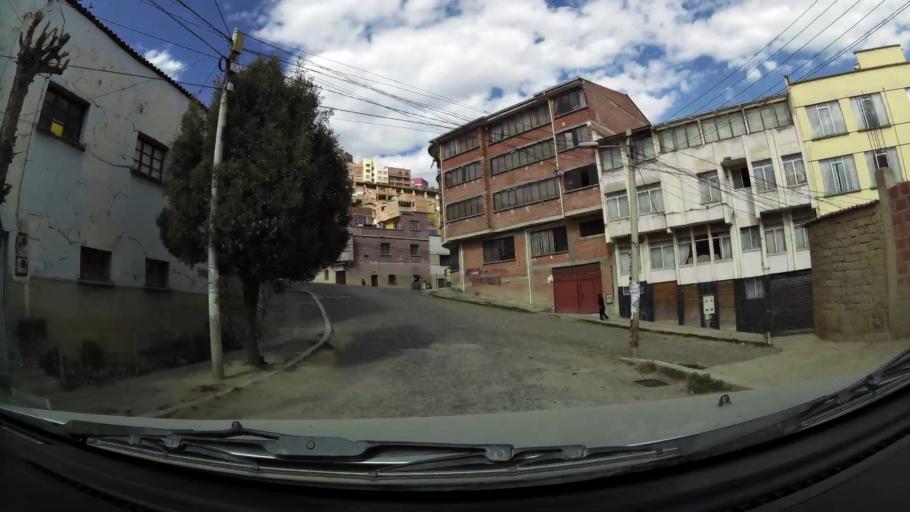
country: BO
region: La Paz
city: La Paz
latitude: -16.4758
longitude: -68.1499
